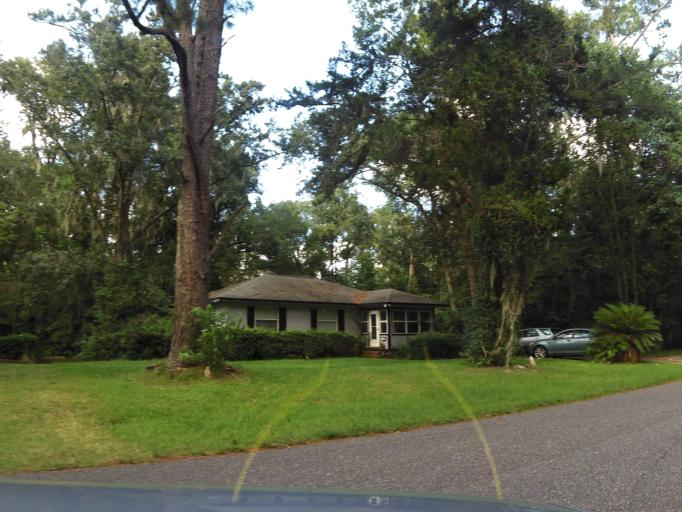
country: US
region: Florida
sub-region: Duval County
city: Jacksonville
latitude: 30.2910
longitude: -81.7282
